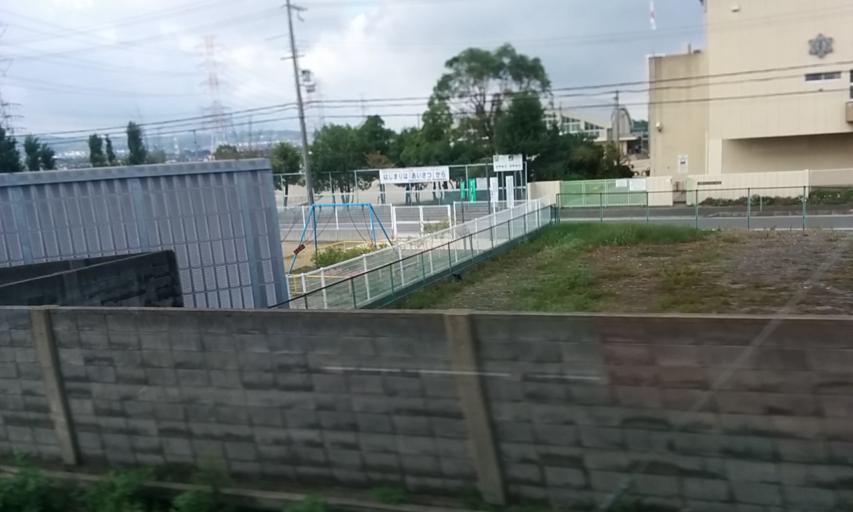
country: JP
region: Kyoto
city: Tanabe
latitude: 34.8449
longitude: 135.7724
